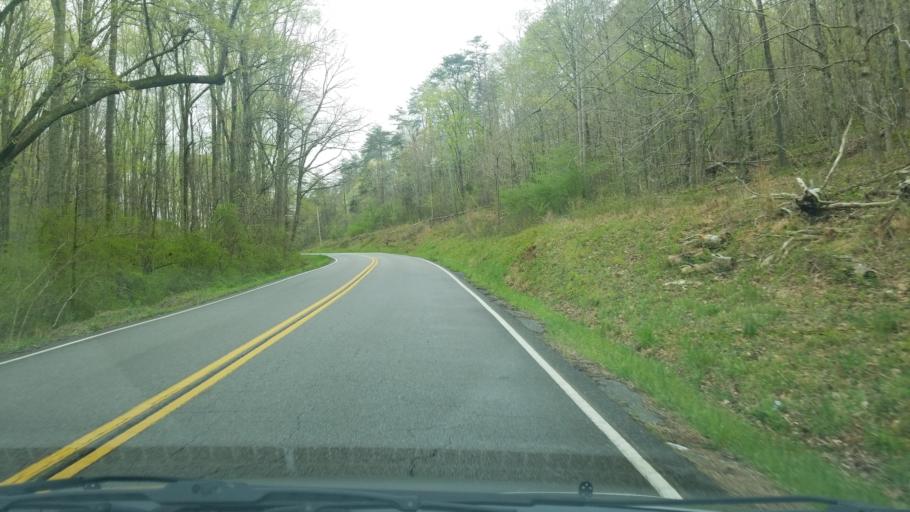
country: US
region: Tennessee
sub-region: Hamilton County
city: Collegedale
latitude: 35.0181
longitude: -85.0721
